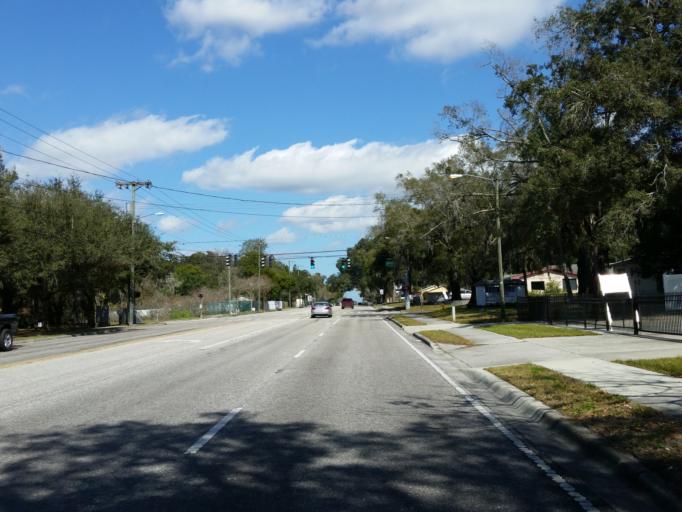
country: US
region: Florida
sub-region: Hillsborough County
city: Brandon
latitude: 27.9517
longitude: -82.2858
